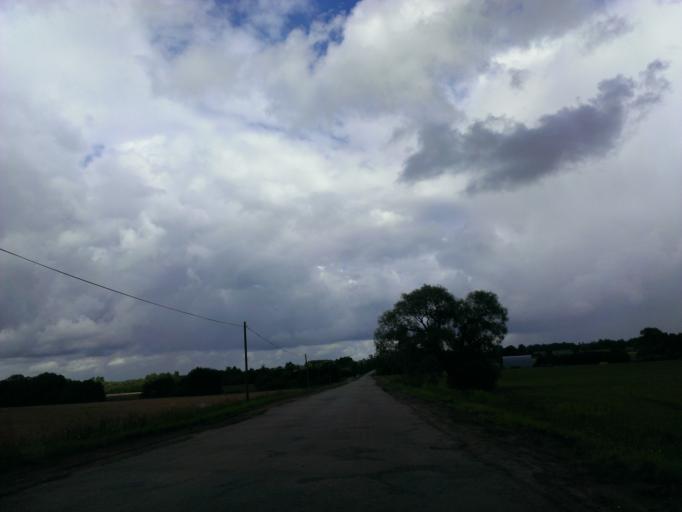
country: LV
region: Sigulda
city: Sigulda
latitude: 57.1621
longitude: 24.9037
